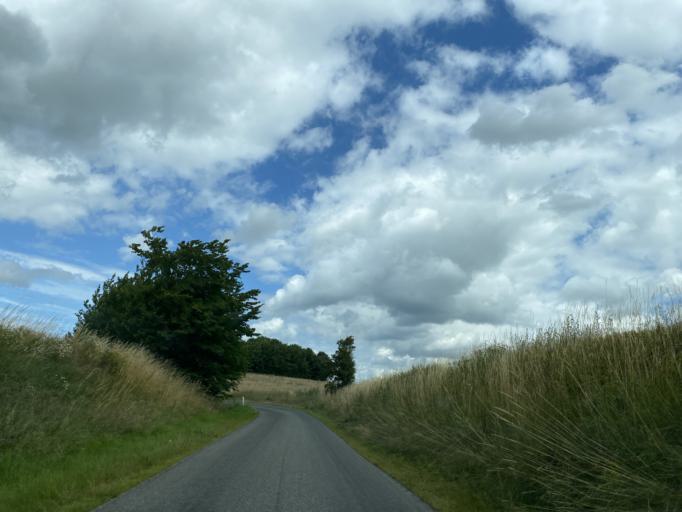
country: DK
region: Central Jutland
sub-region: Silkeborg Kommune
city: Svejbaek
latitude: 56.2357
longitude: 9.6529
